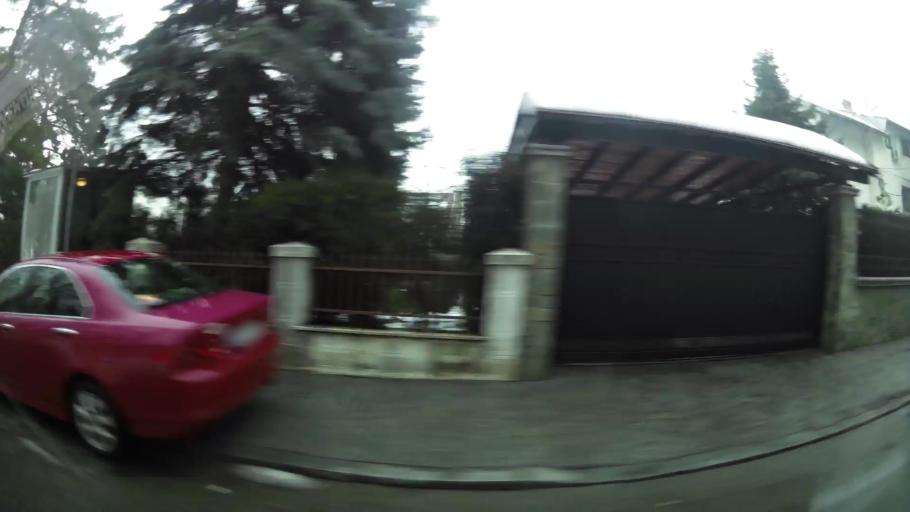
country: RS
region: Central Serbia
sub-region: Belgrade
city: Savski Venac
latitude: 44.7838
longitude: 20.4593
